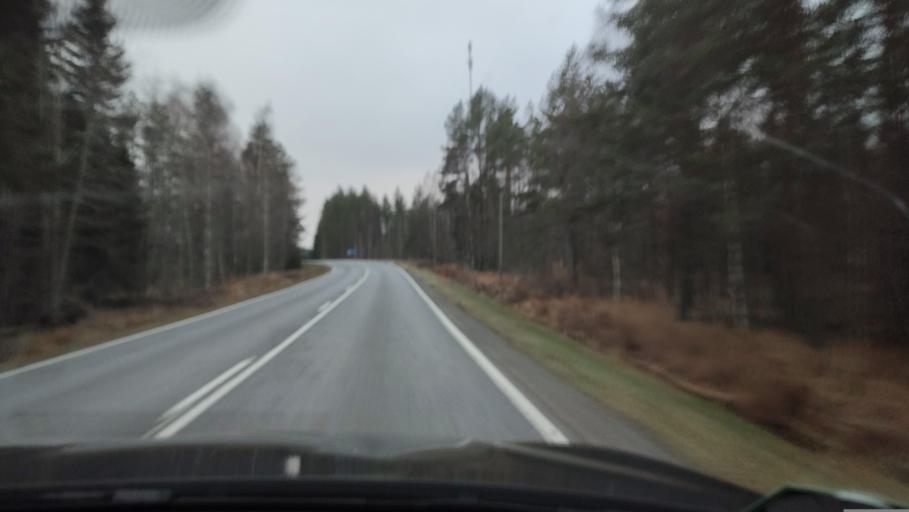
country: FI
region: Southern Ostrobothnia
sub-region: Suupohja
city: Karijoki
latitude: 62.3244
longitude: 21.8711
